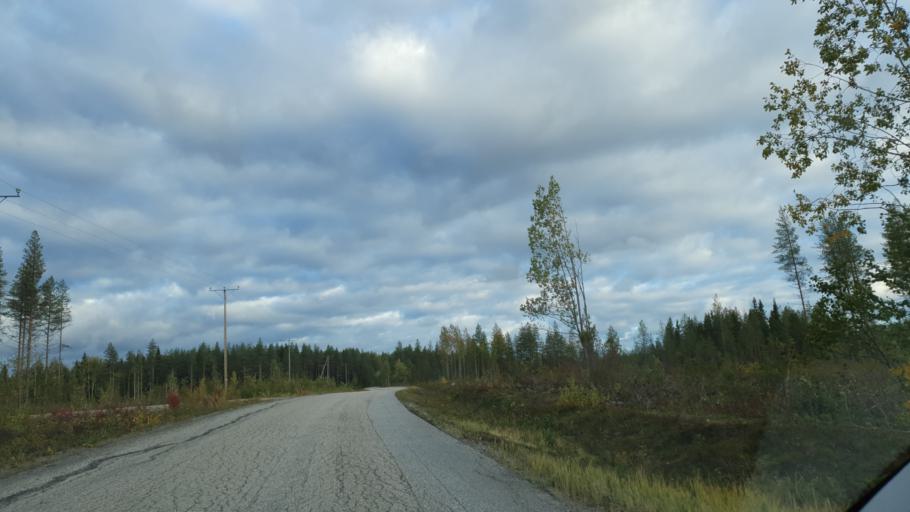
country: FI
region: North Karelia
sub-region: Pielisen Karjala
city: Lieksa
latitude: 63.9152
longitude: 30.1791
